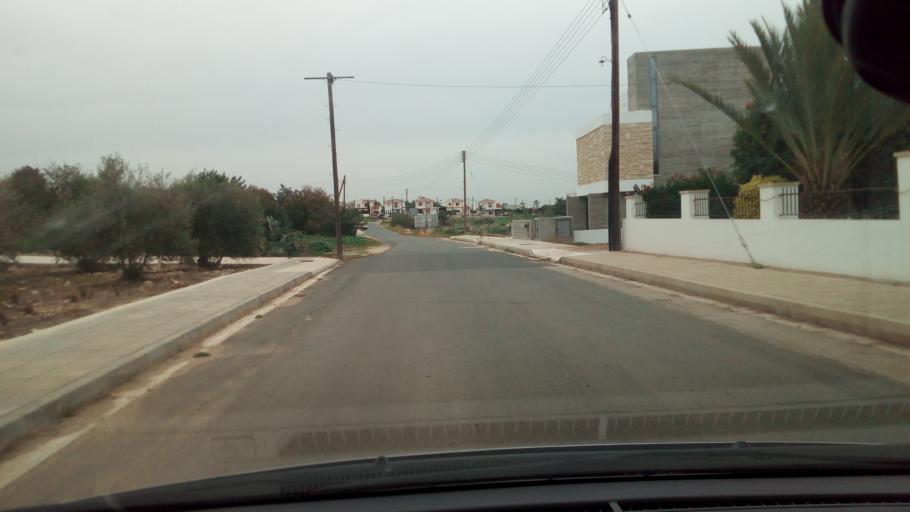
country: CY
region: Pafos
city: Empa
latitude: 34.8011
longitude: 32.4216
